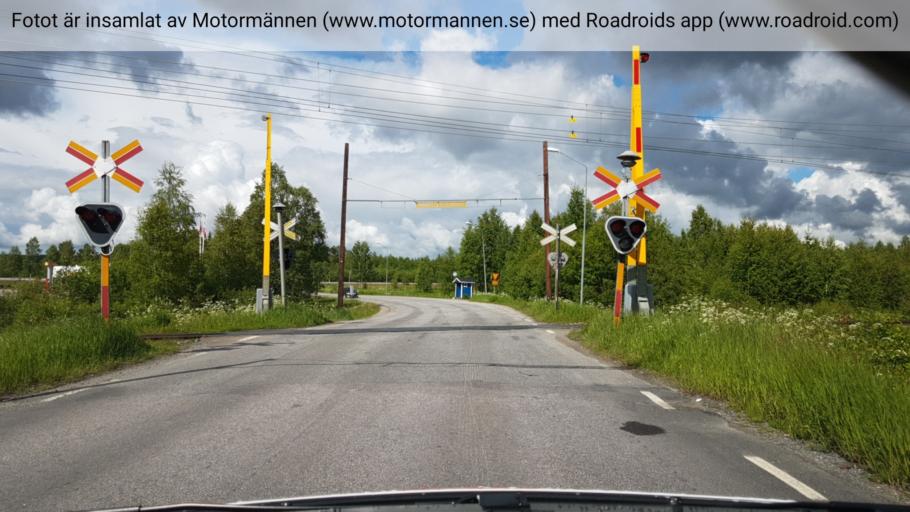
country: SE
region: Vaesterbotten
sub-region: Vannas Kommun
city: Vannasby
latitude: 63.9187
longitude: 19.8464
